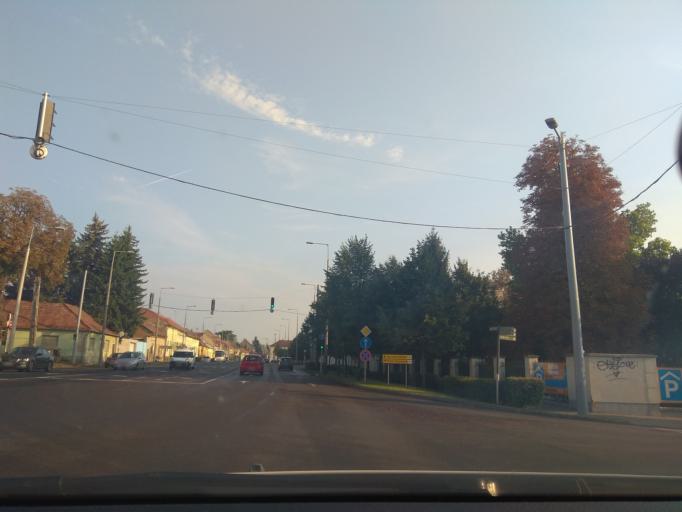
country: HU
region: Heves
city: Eger
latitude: 47.8990
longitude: 20.3675
